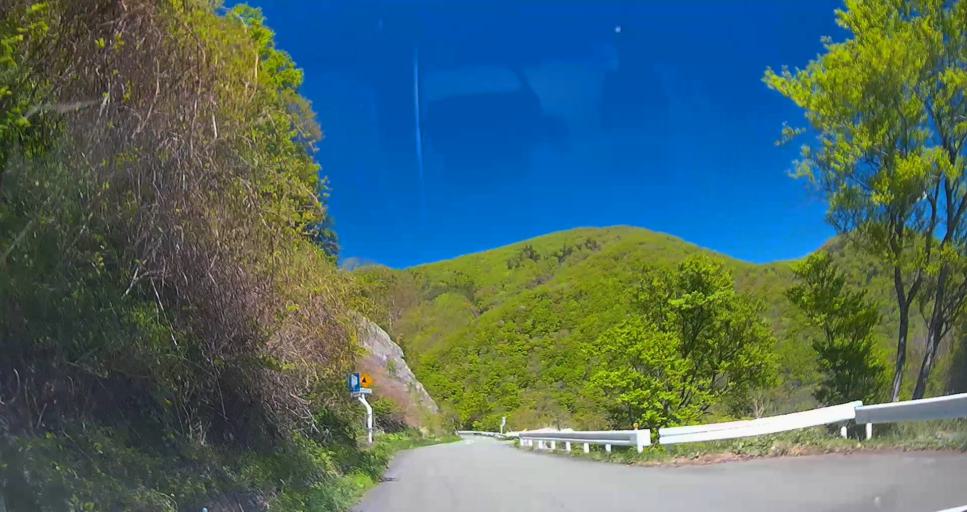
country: JP
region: Aomori
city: Mutsu
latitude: 41.3231
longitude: 140.8167
